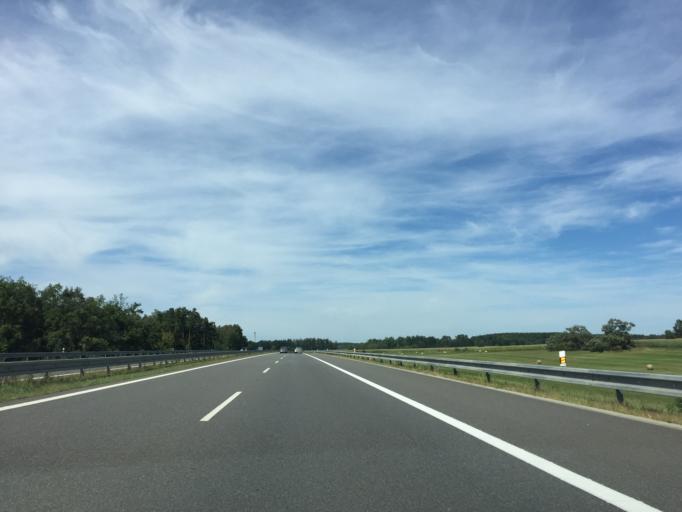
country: CZ
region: Jihocesky
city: Sobeslav
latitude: 49.2306
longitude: 14.7280
